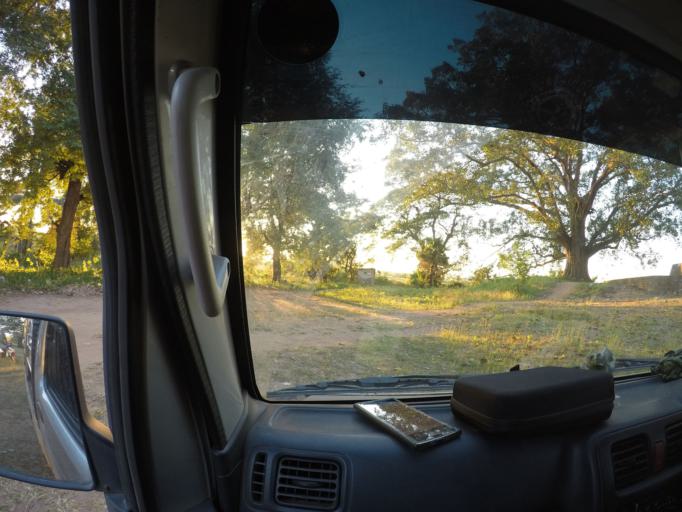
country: MM
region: Bago
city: Pyay
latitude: 18.8341
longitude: 95.3019
